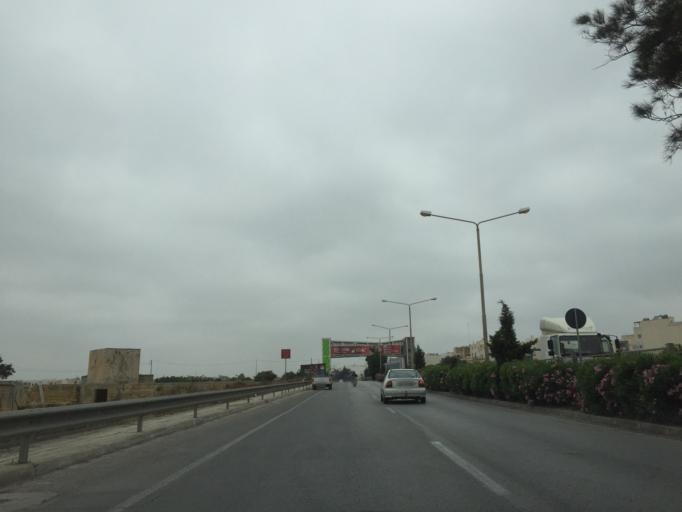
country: MT
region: Saint Venera
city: Santa Venera
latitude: 35.8846
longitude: 14.4710
